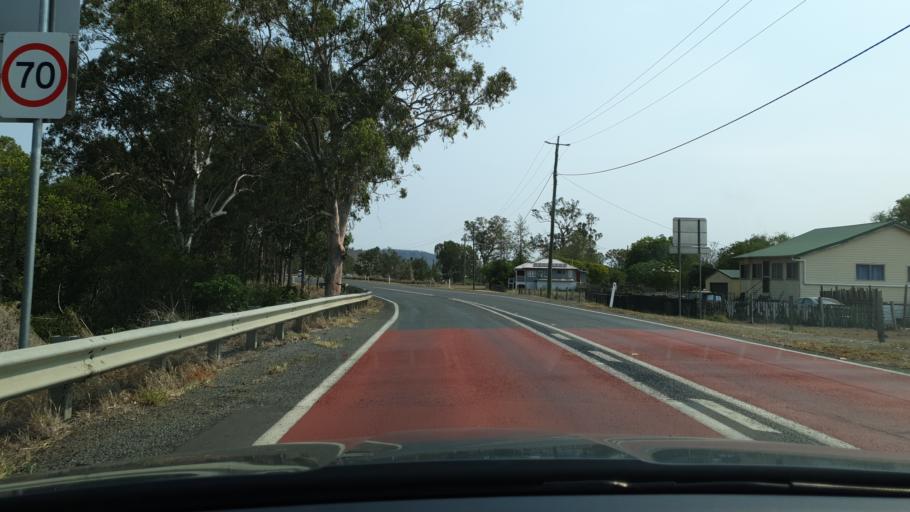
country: AU
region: Queensland
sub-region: Ipswich
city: Deebing Heights
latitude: -28.0055
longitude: 152.6806
